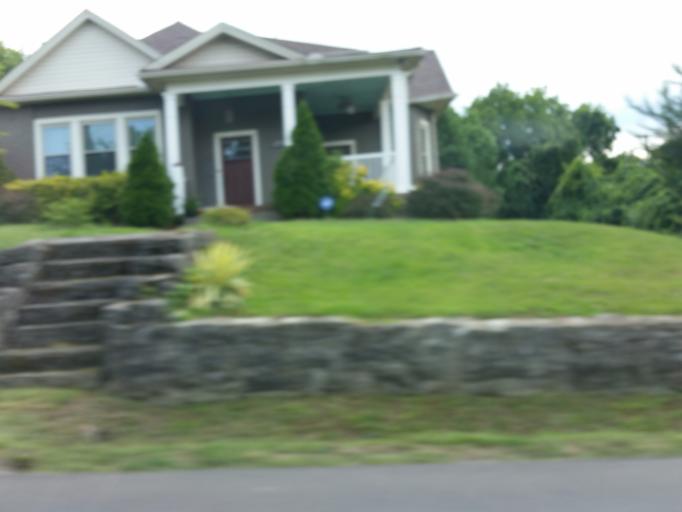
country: US
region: Tennessee
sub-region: Davidson County
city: Nashville
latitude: 36.1822
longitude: -86.7312
